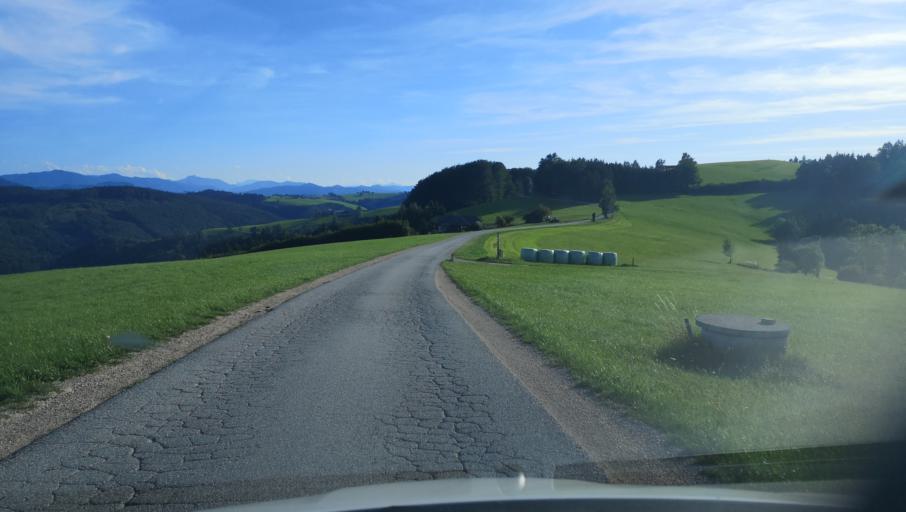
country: AT
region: Lower Austria
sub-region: Politischer Bezirk Amstetten
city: Euratsfeld
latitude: 48.0226
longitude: 14.9089
